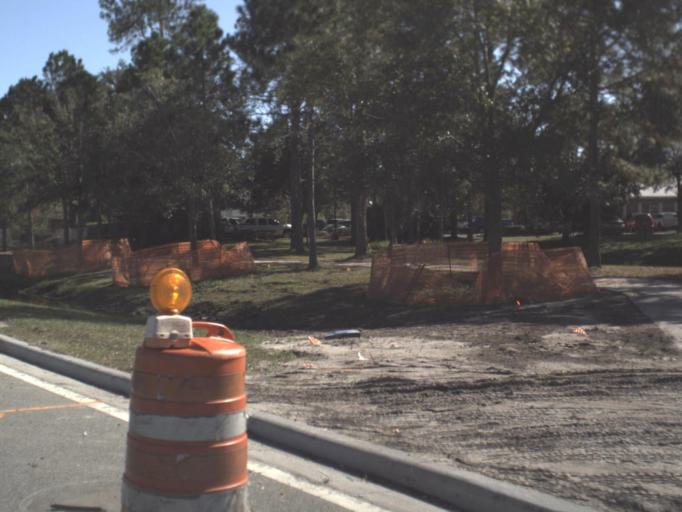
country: US
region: Florida
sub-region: Flagler County
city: Palm Coast
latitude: 29.5533
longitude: -81.2261
